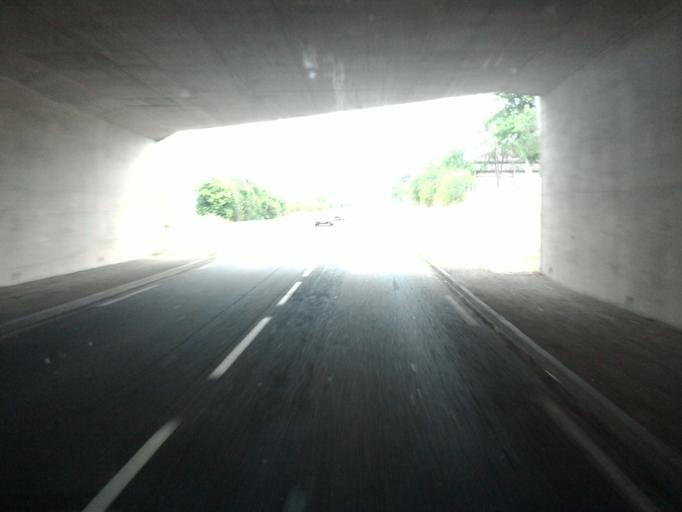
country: FR
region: Lorraine
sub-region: Departement de Meurthe-et-Moselle
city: Colombey-les-Belles
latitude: 48.5392
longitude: 5.9031
